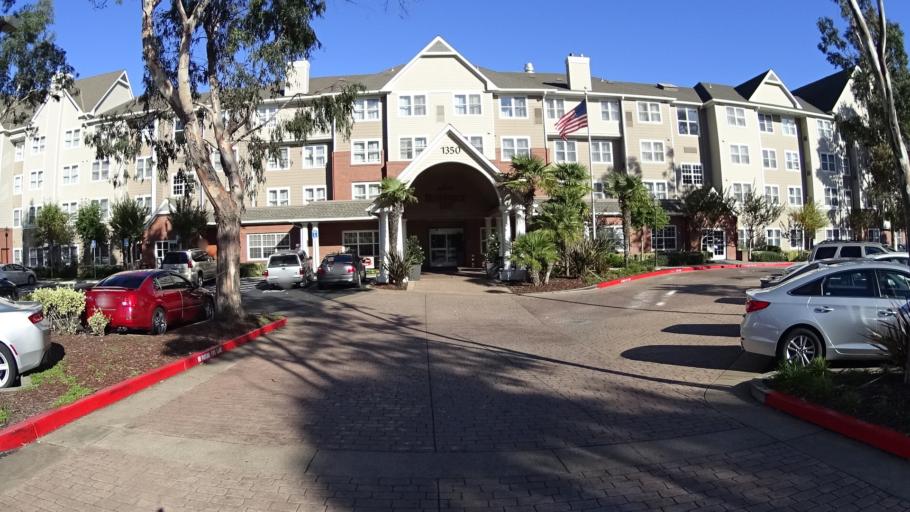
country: US
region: California
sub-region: San Mateo County
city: Brisbane
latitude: 37.6669
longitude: -122.3939
